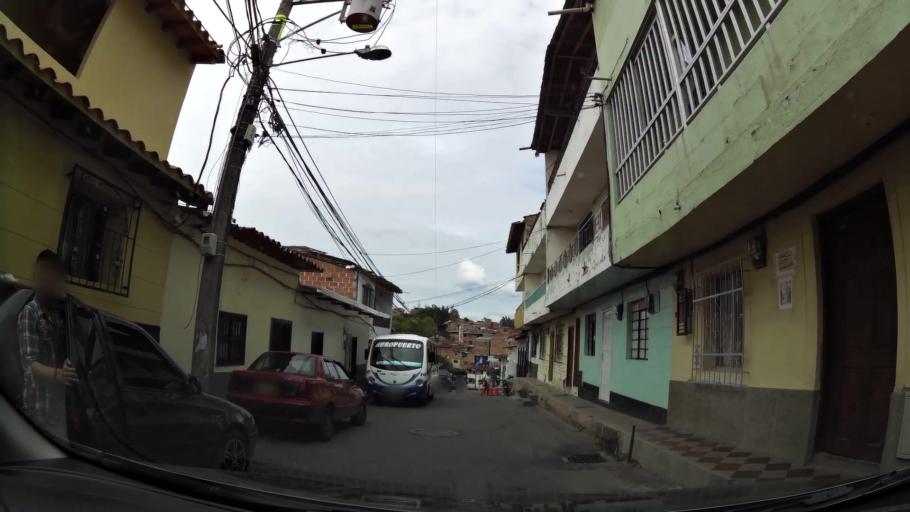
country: CO
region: Antioquia
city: Rionegro
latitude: 6.1563
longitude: -75.3756
